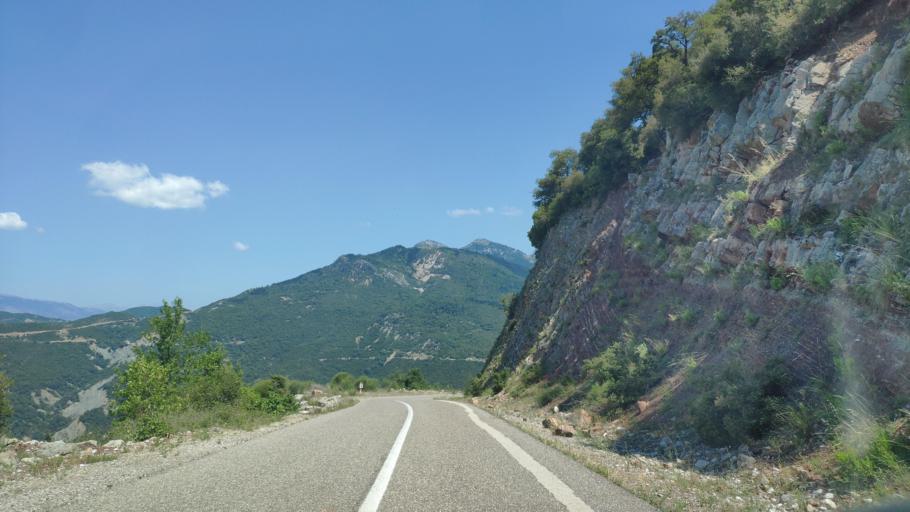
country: GR
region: Central Greece
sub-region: Nomos Evrytanias
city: Kerasochori
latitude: 39.0071
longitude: 21.5942
